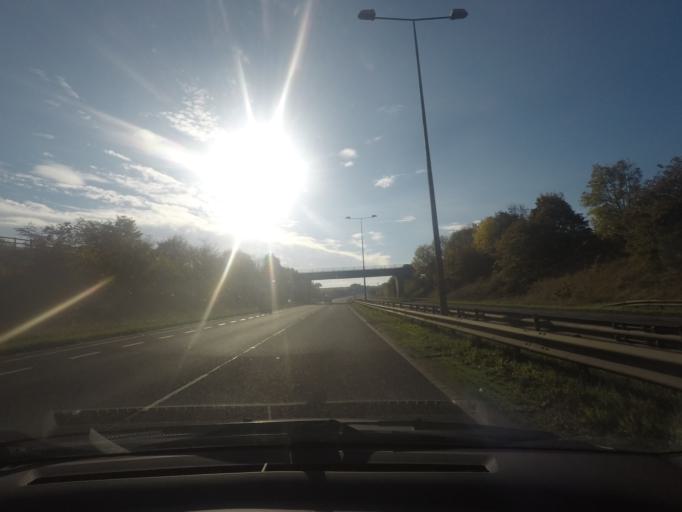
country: GB
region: England
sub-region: North Lincolnshire
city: Barton upon Humber
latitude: 53.6745
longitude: -0.4532
